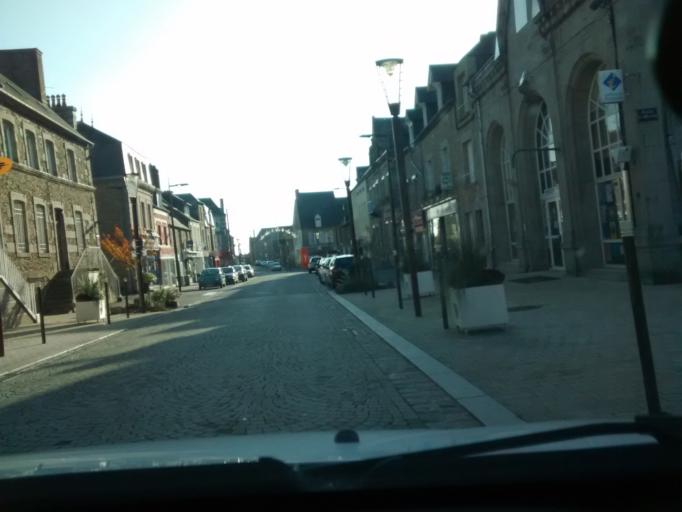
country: FR
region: Lower Normandy
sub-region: Departement de la Manche
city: Pontorson
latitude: 48.5539
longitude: -1.5094
